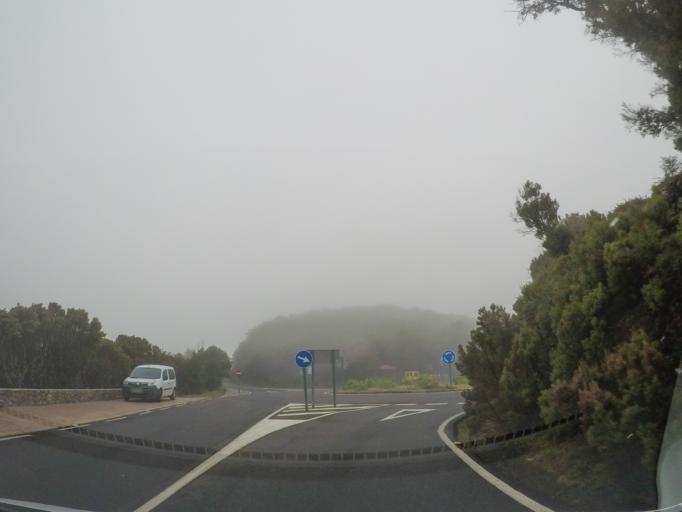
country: ES
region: Canary Islands
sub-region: Provincia de Santa Cruz de Tenerife
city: Alajero
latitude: 28.1086
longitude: -17.2421
